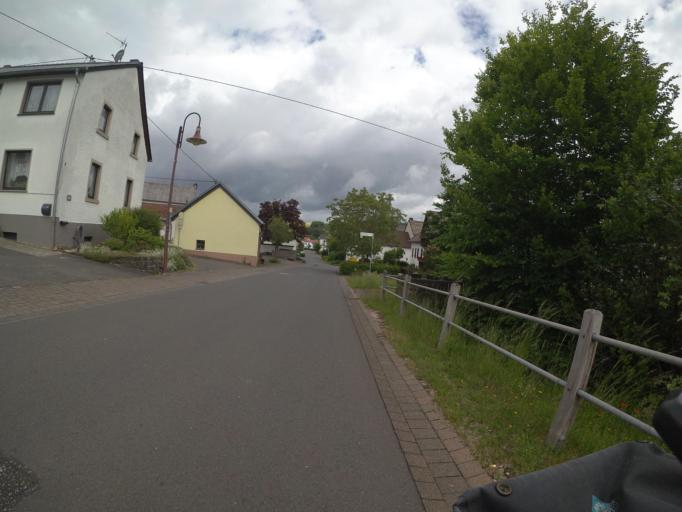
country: DE
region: Rheinland-Pfalz
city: Hinterweiler
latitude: 50.2361
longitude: 6.7557
